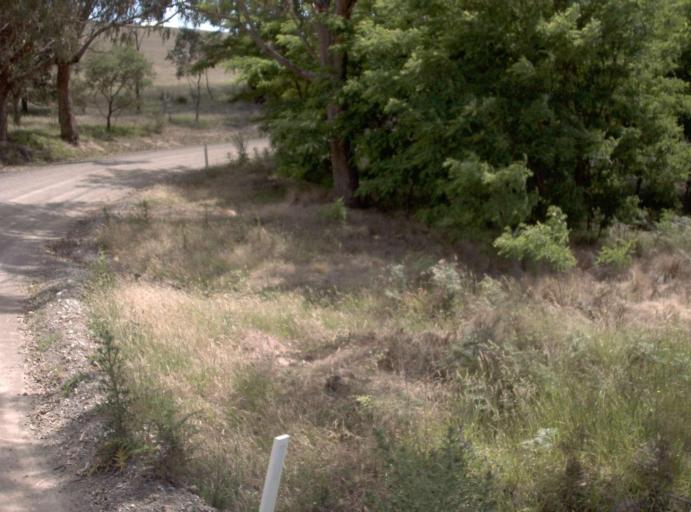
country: AU
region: New South Wales
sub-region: Bombala
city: Bombala
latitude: -37.1435
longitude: 148.6677
